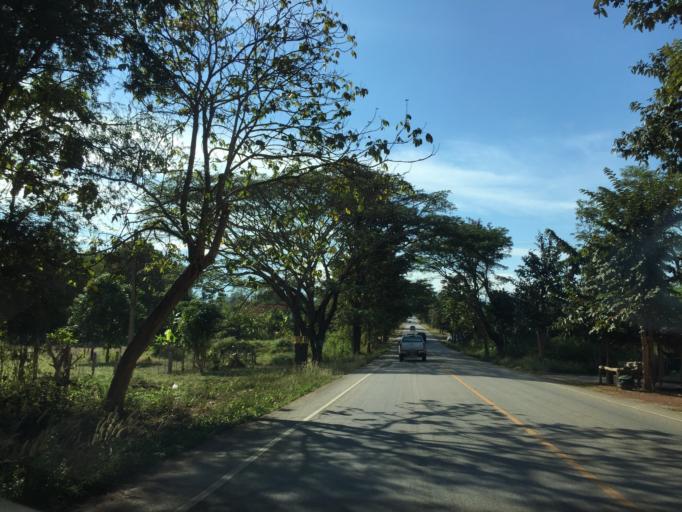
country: TH
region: Loei
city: Wang Saphung
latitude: 17.3153
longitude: 101.7408
